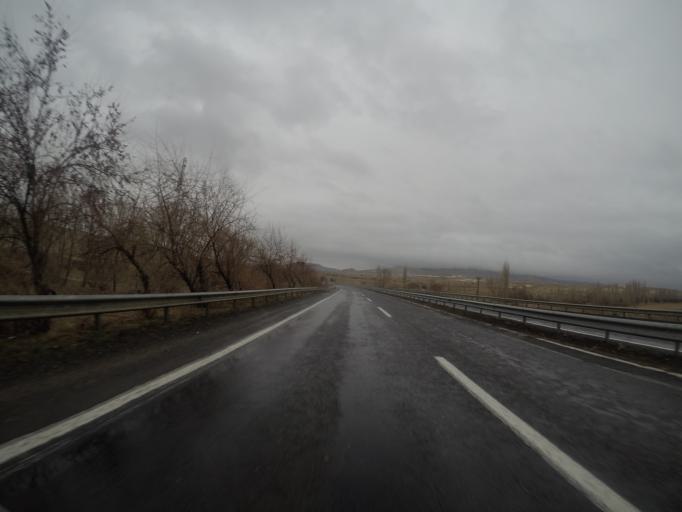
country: TR
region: Nevsehir
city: Avanos
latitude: 38.7122
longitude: 34.9119
